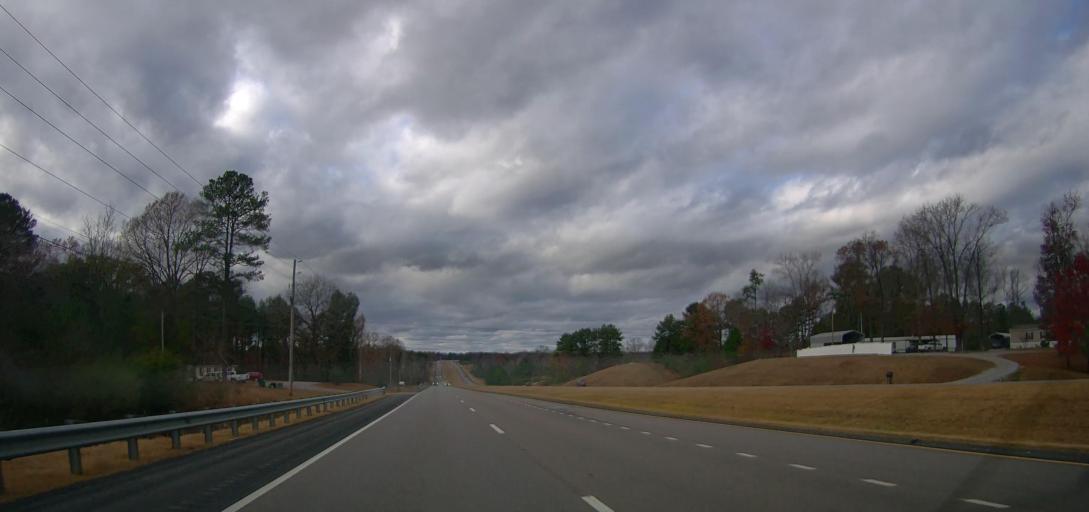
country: US
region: Alabama
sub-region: Morgan County
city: Falkville
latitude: 34.2533
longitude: -86.9731
